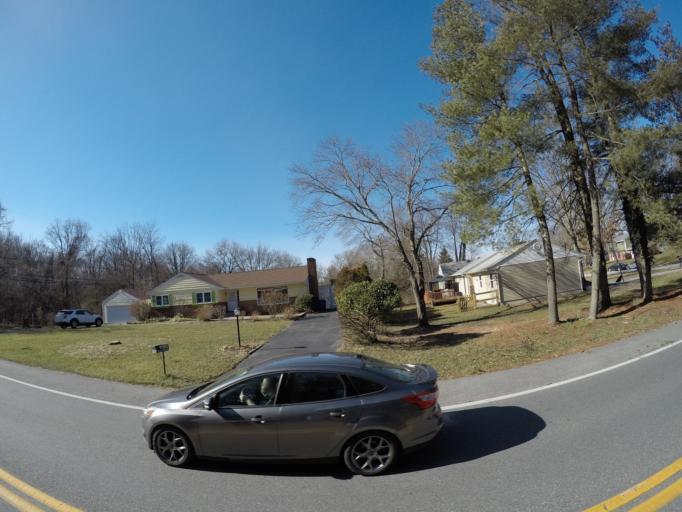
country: US
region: Maryland
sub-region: Howard County
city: Columbia
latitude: 39.2408
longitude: -76.8310
